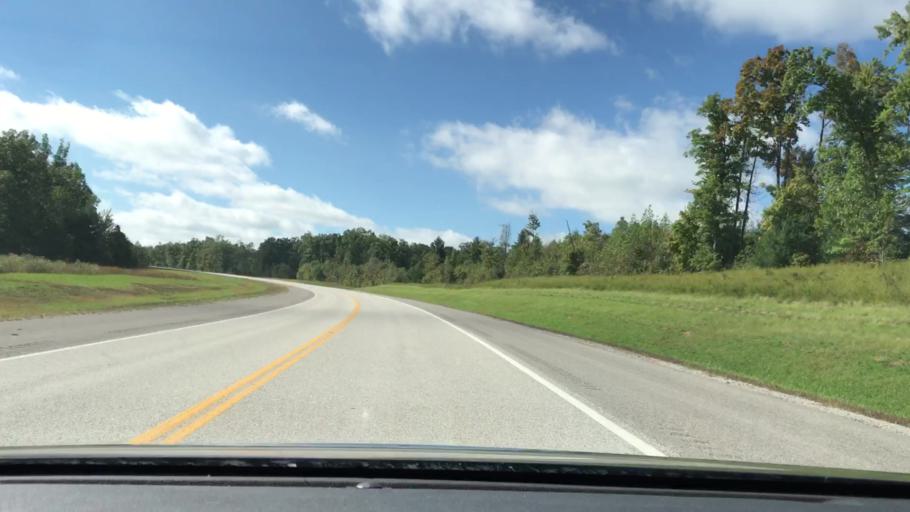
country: US
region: Tennessee
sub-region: Scott County
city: Huntsville
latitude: 36.3514
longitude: -84.7077
